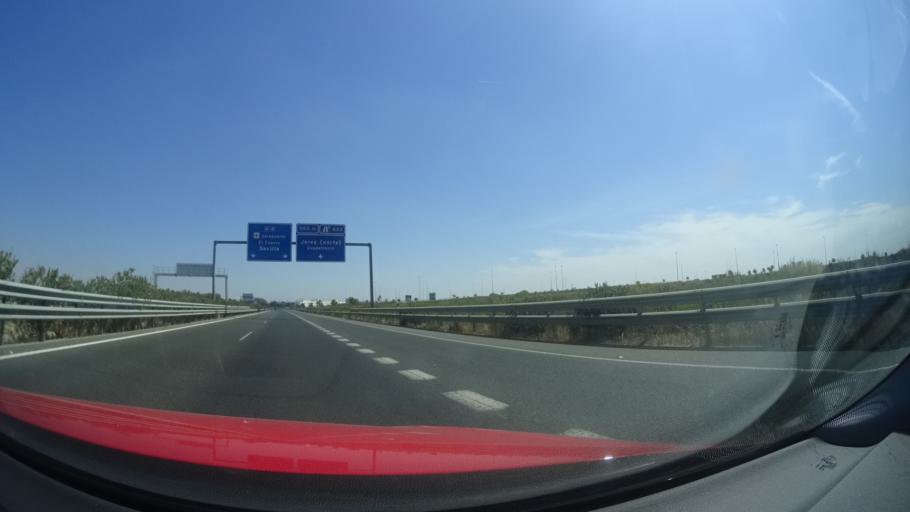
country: ES
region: Andalusia
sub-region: Provincia de Cadiz
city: Jerez de la Frontera
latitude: 36.7162
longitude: -6.1158
